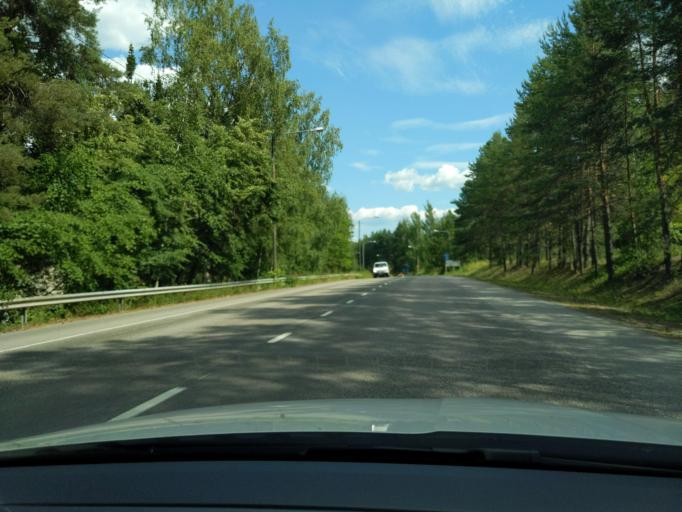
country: FI
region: Paijanne Tavastia
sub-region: Lahti
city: Heinola
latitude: 61.1963
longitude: 26.0232
